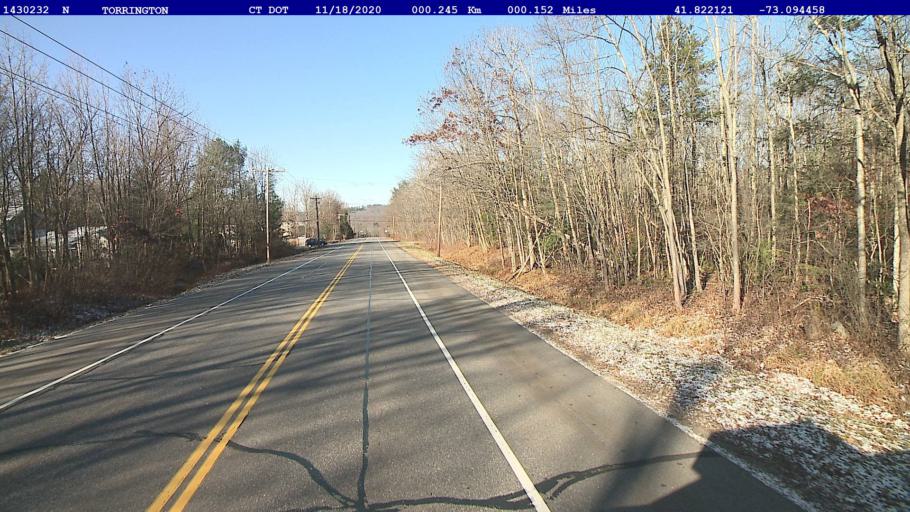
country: US
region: Connecticut
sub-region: Litchfield County
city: Torrington
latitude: 41.8221
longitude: -73.0944
